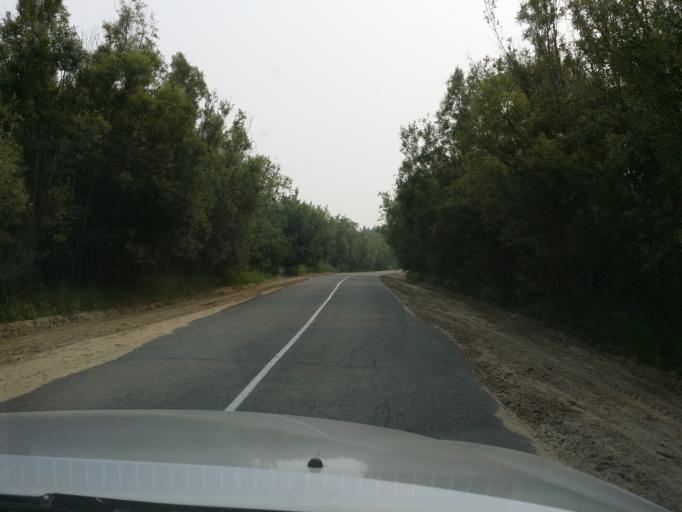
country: RU
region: Khanty-Mansiyskiy Avtonomnyy Okrug
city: Megion
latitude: 60.9832
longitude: 76.2972
